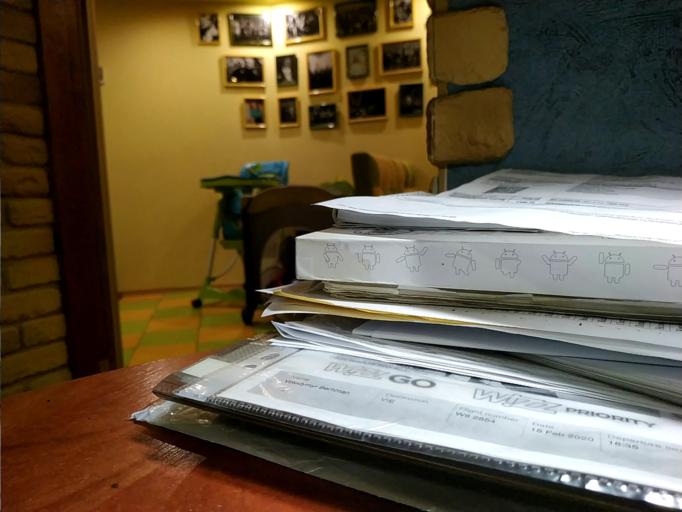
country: RU
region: Arkhangelskaya
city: Voloshka
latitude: 61.1304
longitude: 39.5409
